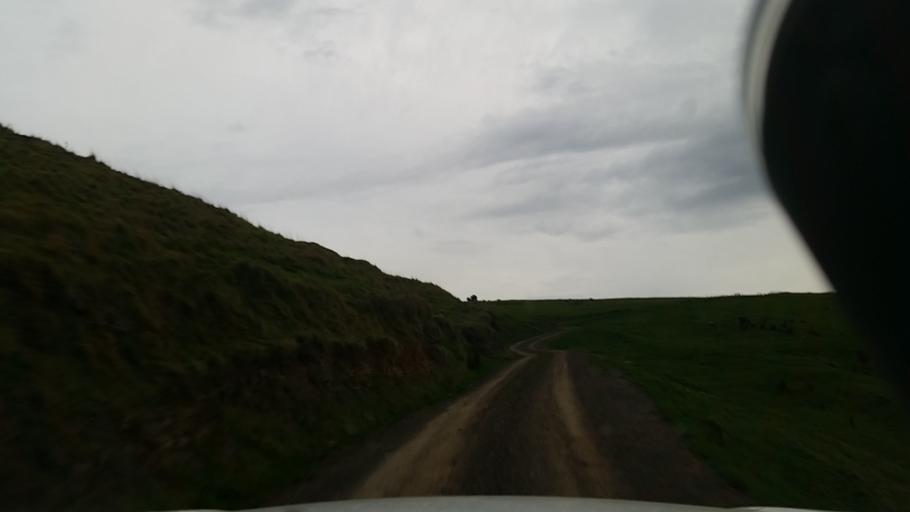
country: NZ
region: Canterbury
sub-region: Christchurch City
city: Christchurch
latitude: -43.8727
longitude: 173.0020
